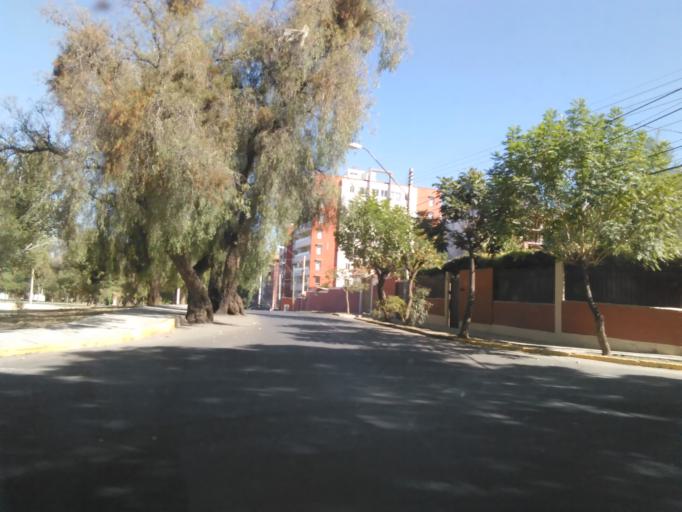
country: BO
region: Cochabamba
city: Cochabamba
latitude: -17.3711
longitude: -66.1453
